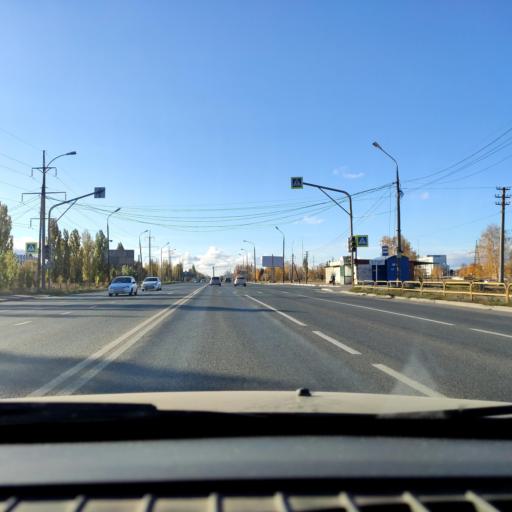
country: RU
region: Samara
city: Tol'yatti
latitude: 53.5635
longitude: 49.2900
